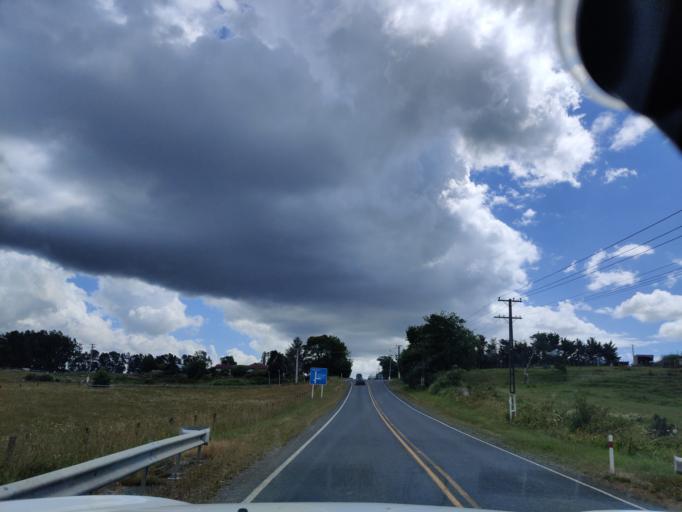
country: NZ
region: Auckland
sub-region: Auckland
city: Red Hill
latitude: -37.0395
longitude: 174.9908
